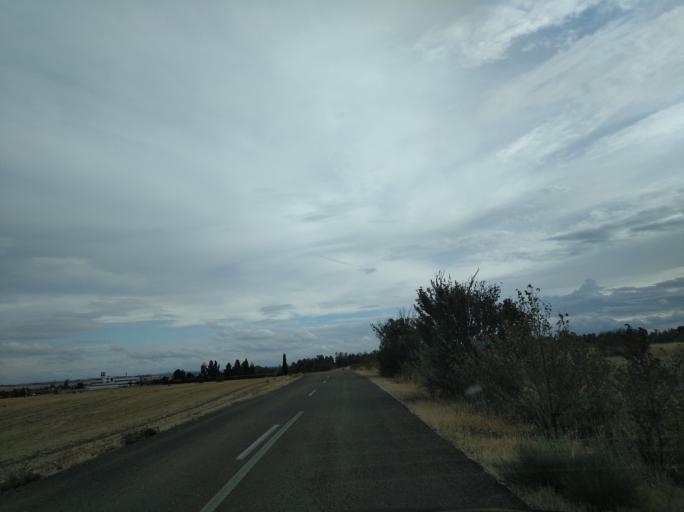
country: ES
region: Extremadura
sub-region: Provincia de Badajoz
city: Badajoz
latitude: 38.8955
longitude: -7.0170
